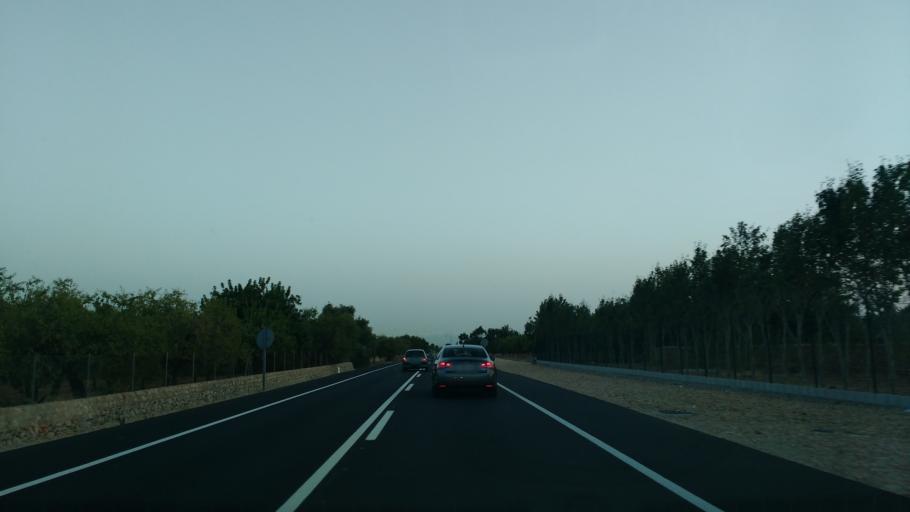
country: ES
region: Balearic Islands
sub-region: Illes Balears
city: Bunyola
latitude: 39.6729
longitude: 2.6783
